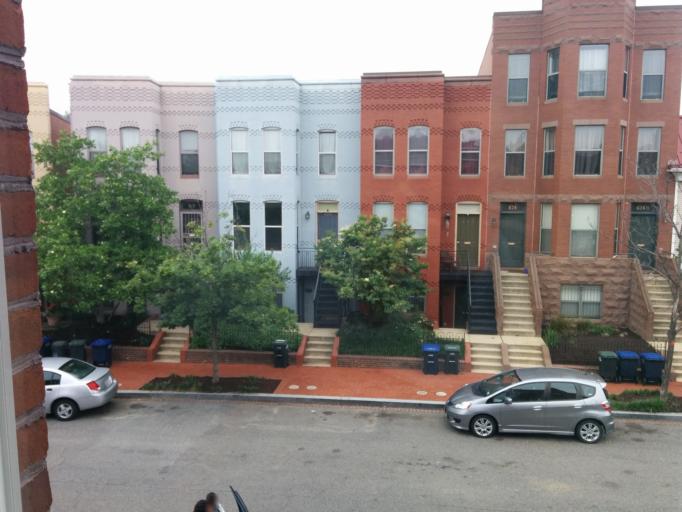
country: US
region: Washington, D.C.
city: Washington, D.C.
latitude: 38.8800
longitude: -76.9976
